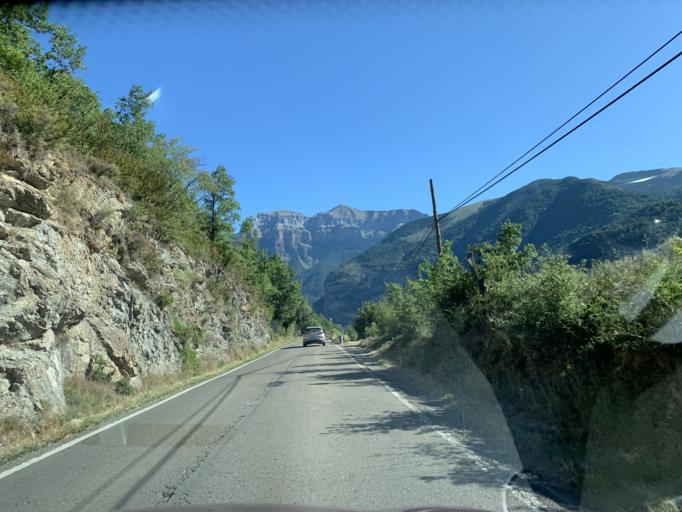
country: ES
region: Aragon
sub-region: Provincia de Huesca
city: Broto
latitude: 42.6171
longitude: -0.1167
